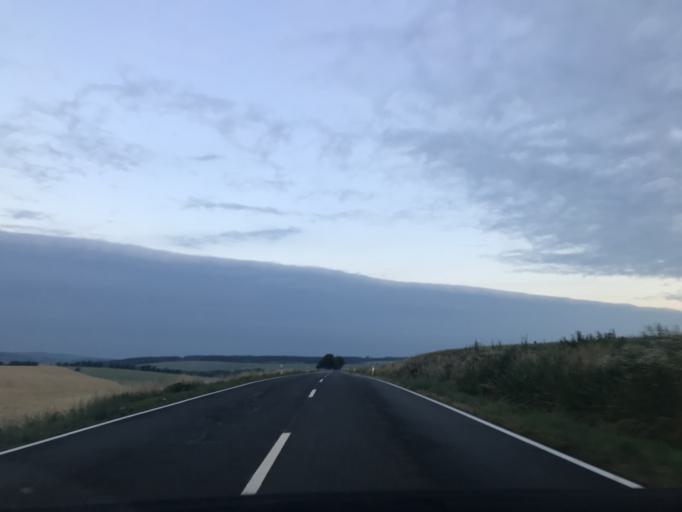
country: DE
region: Thuringia
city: Niederorschel
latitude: 51.3551
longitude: 10.4325
